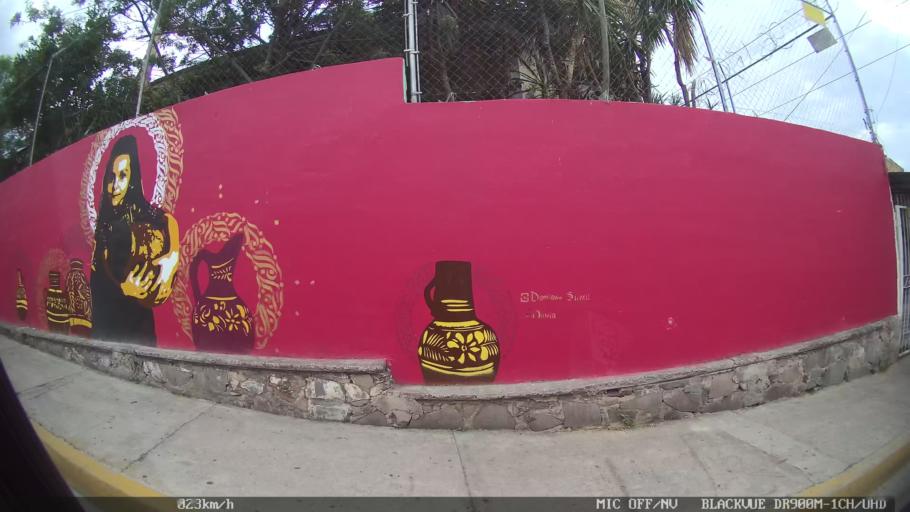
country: MX
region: Jalisco
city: Tonala
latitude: 20.6210
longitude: -103.2653
